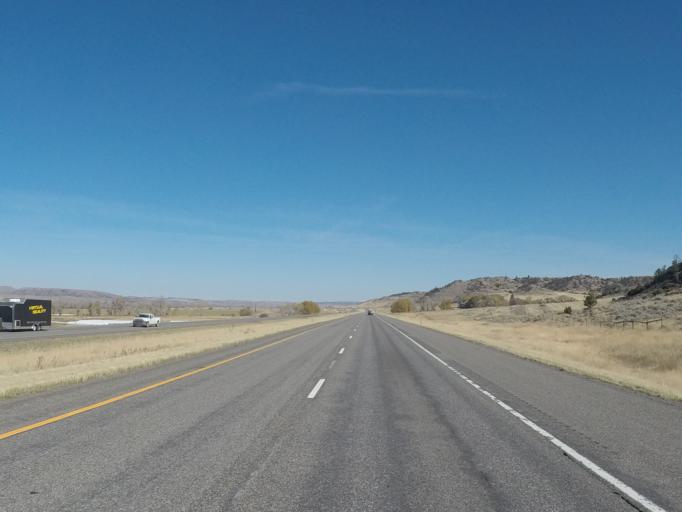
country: US
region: Montana
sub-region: Sweet Grass County
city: Big Timber
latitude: 45.7725
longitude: -110.0770
